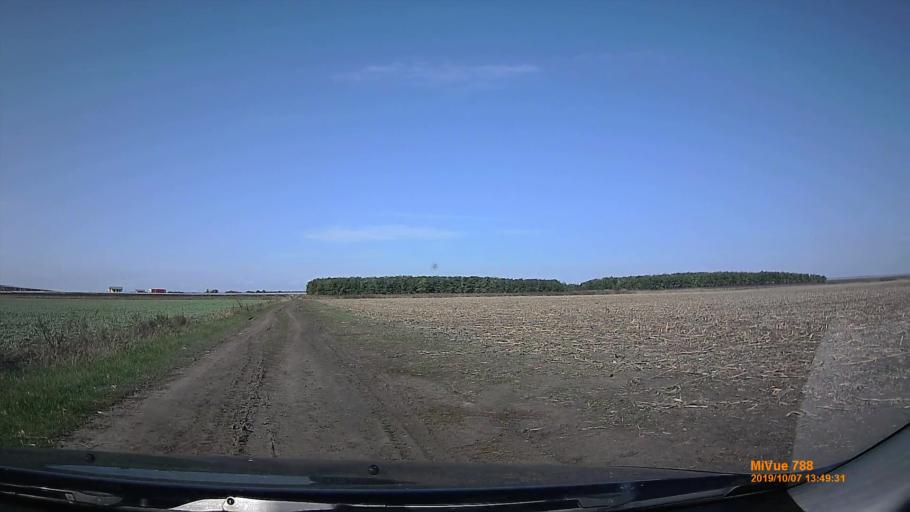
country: HU
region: Jasz-Nagykun-Szolnok
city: Cserkeszolo
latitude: 46.8802
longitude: 20.2185
